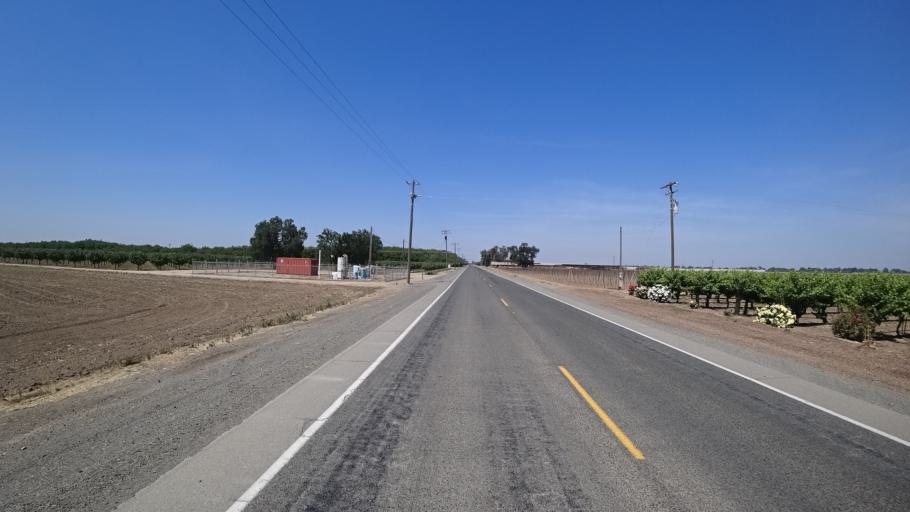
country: US
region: California
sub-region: Fresno County
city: Laton
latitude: 36.4011
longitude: -119.7243
